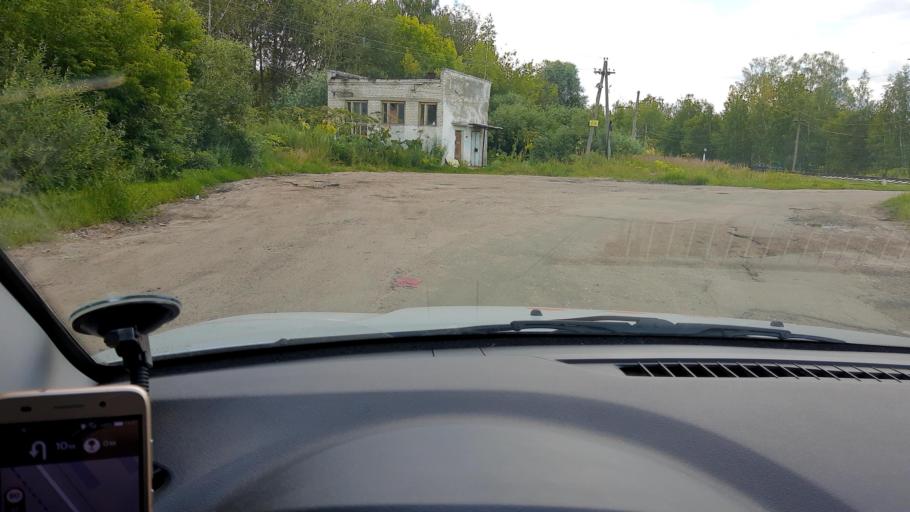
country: RU
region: Nizjnij Novgorod
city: Afonino
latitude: 56.2024
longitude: 44.0313
